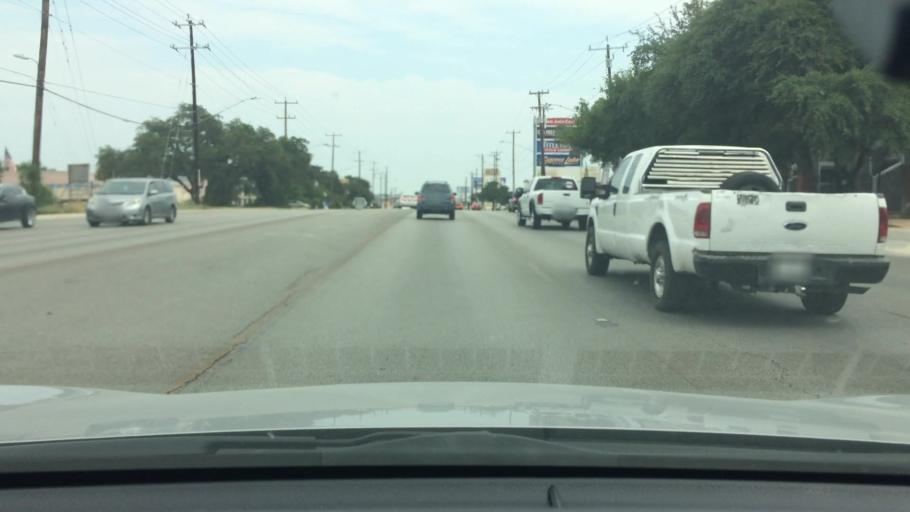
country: US
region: Texas
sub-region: Bexar County
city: Leon Valley
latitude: 29.4615
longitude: -98.6412
